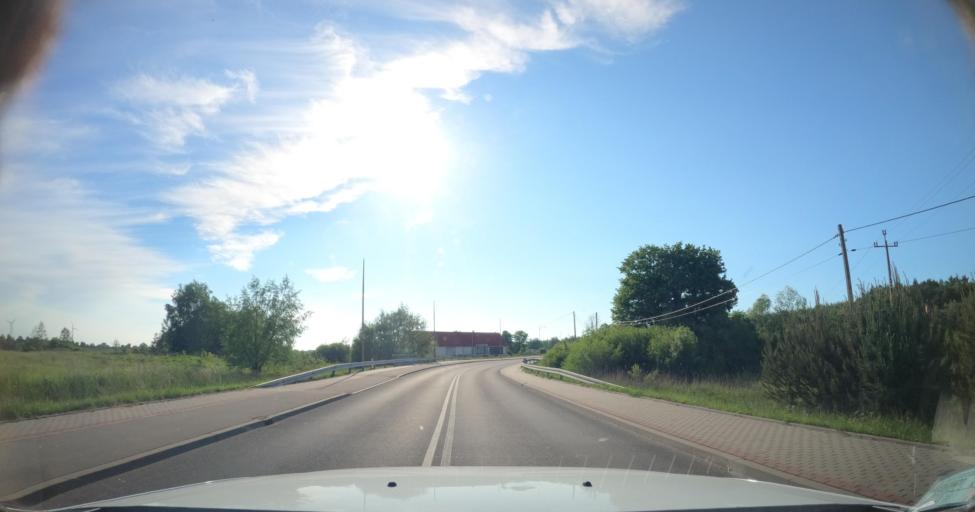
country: PL
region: Warmian-Masurian Voivodeship
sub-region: Powiat elblaski
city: Paslek
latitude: 54.0732
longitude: 19.6414
